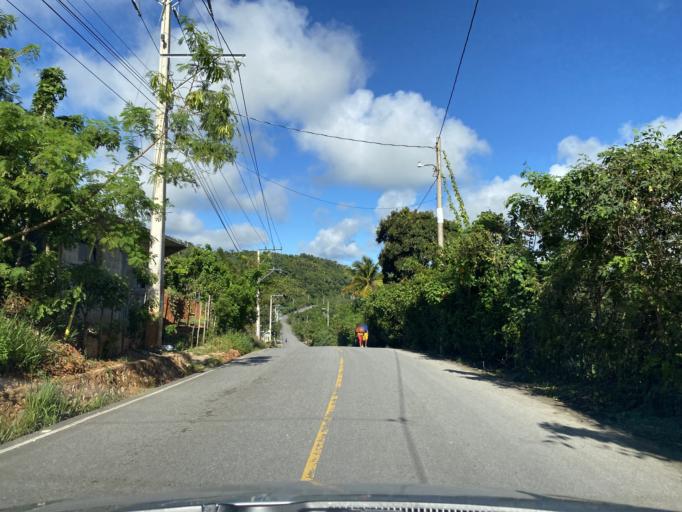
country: DO
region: Samana
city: Sanchez
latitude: 19.2526
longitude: -69.5821
